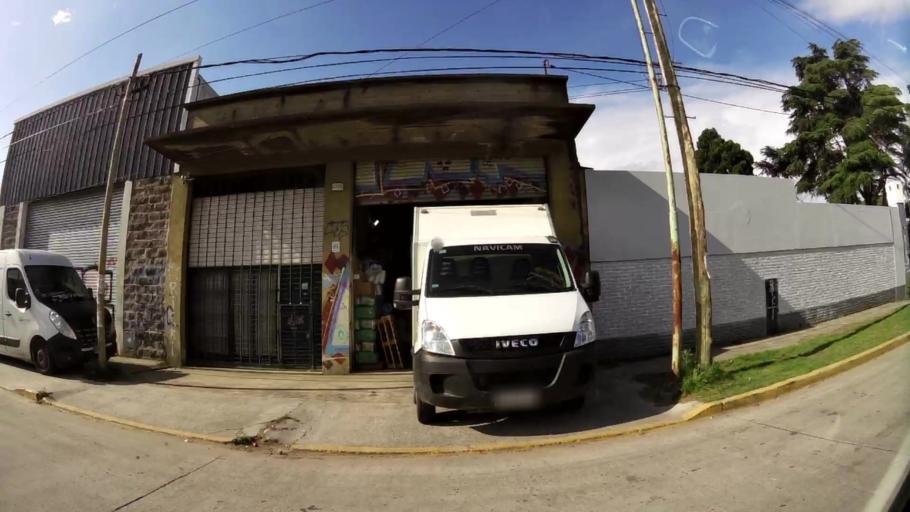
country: AR
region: Buenos Aires
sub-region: Partido de Merlo
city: Merlo
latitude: -34.6663
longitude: -58.7153
